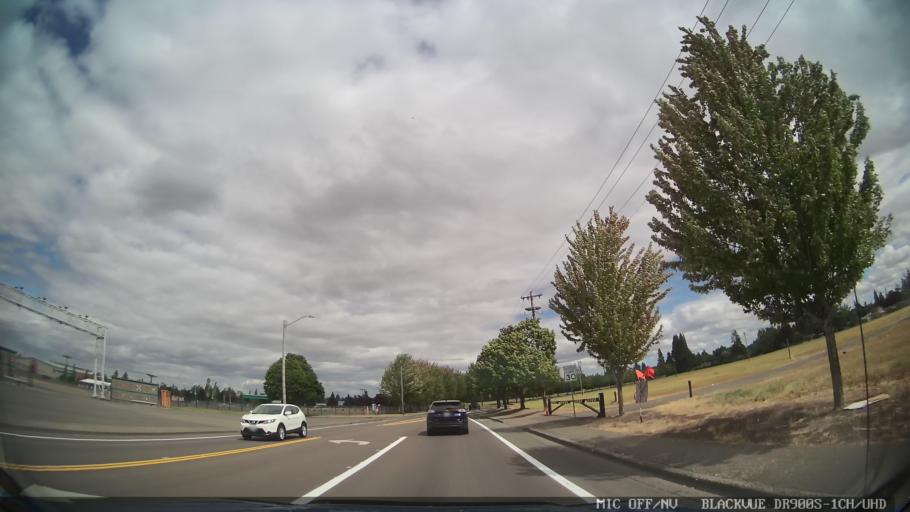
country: US
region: Oregon
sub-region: Marion County
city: Salem
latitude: 44.9562
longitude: -123.0097
